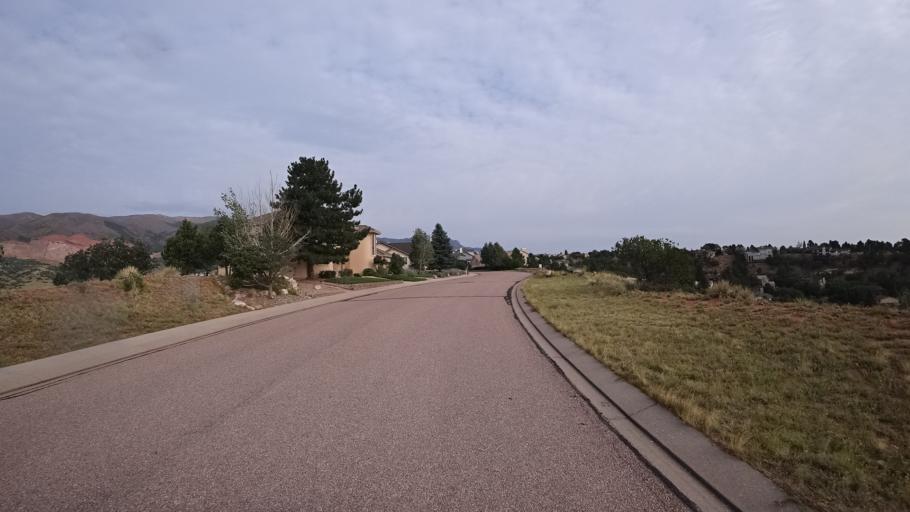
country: US
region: Colorado
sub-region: El Paso County
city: Air Force Academy
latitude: 38.9324
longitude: -104.8605
